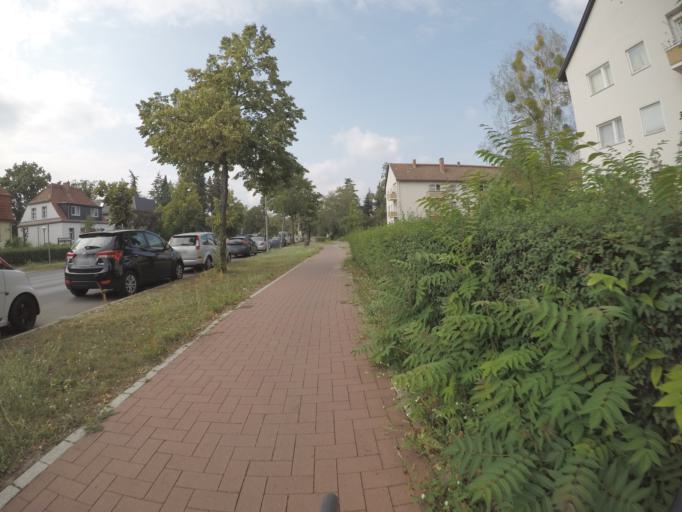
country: DE
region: Brandenburg
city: Teltow
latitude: 52.4135
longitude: 13.2668
